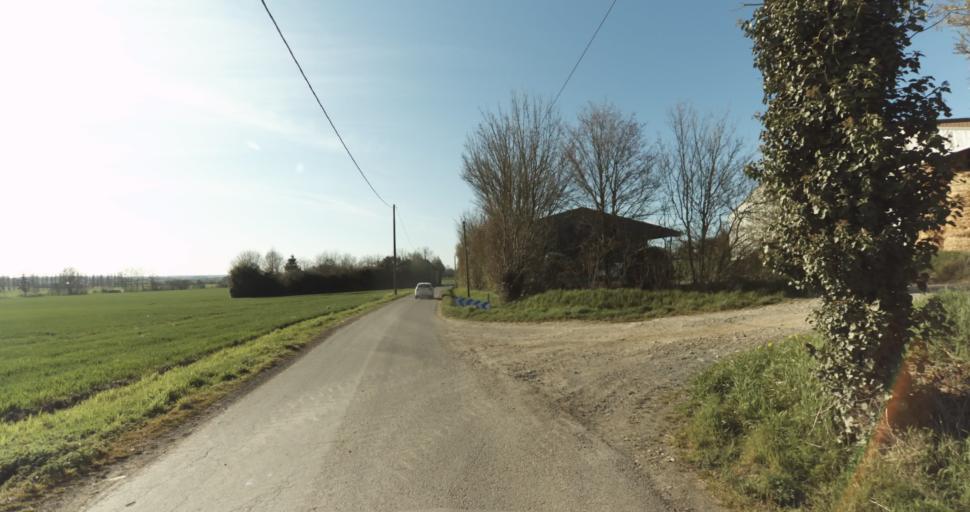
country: FR
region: Lower Normandy
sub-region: Departement du Calvados
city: Saint-Pierre-sur-Dives
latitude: 49.0419
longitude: 0.0330
